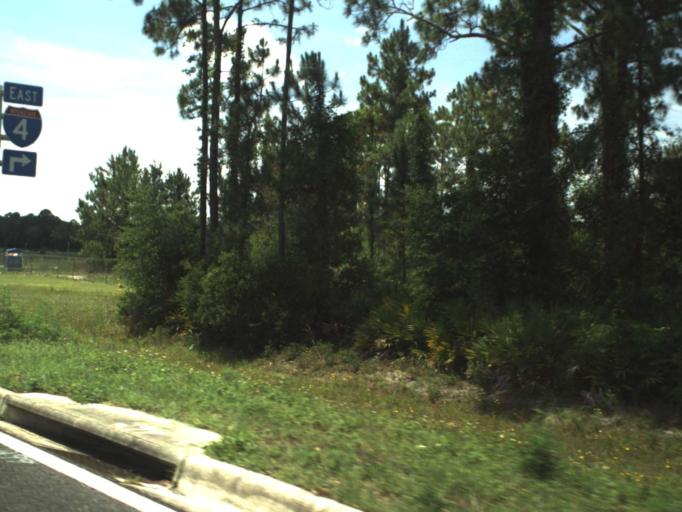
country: US
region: Florida
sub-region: Volusia County
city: Lake Helen
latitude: 29.0180
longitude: -81.2265
